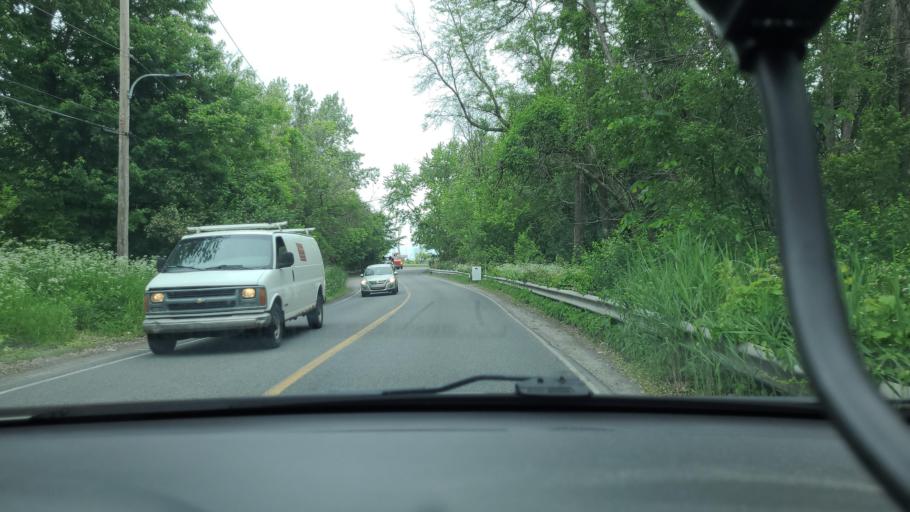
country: CA
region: Quebec
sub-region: Lanaudiere
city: Charlemagne
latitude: 45.6980
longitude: -73.5035
